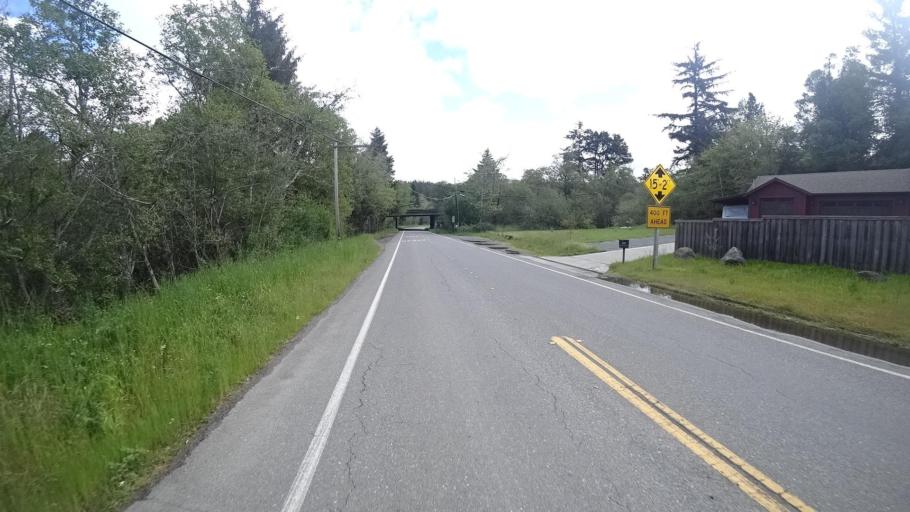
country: US
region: California
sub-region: Humboldt County
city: Blue Lake
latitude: 40.9027
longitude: -124.0288
